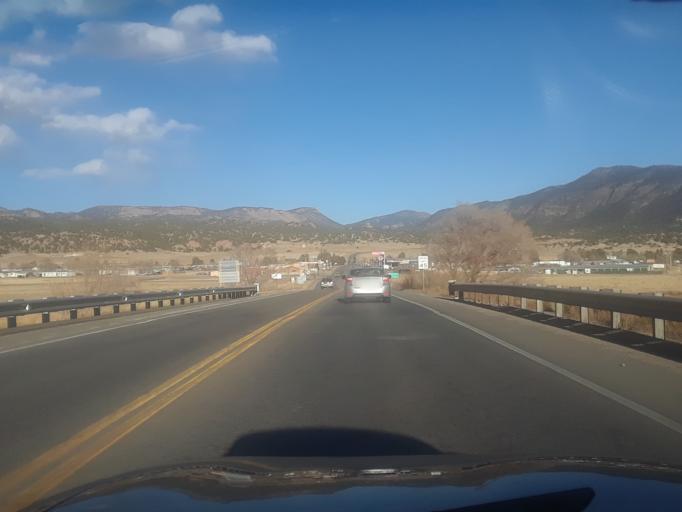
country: US
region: Colorado
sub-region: Chaffee County
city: Buena Vista
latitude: 38.8105
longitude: -106.1132
